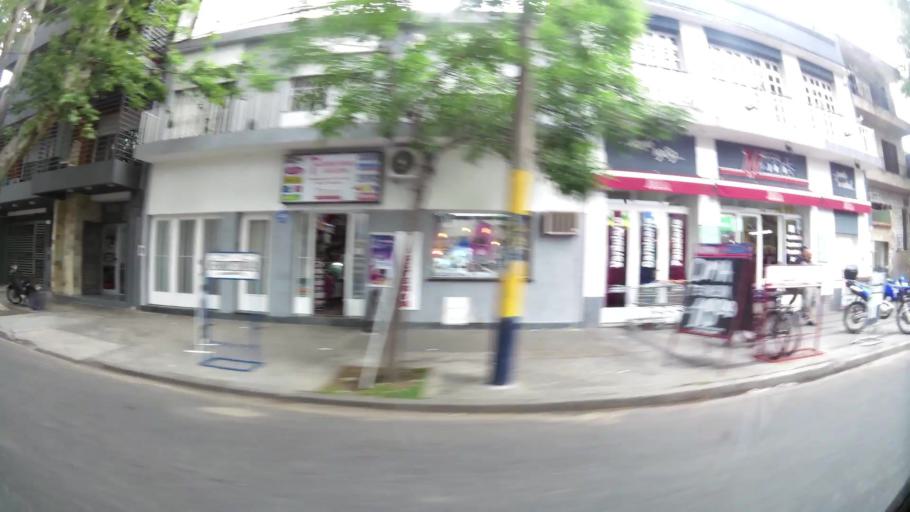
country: AR
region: Santa Fe
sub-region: Departamento de Rosario
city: Rosario
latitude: -32.9152
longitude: -60.6837
